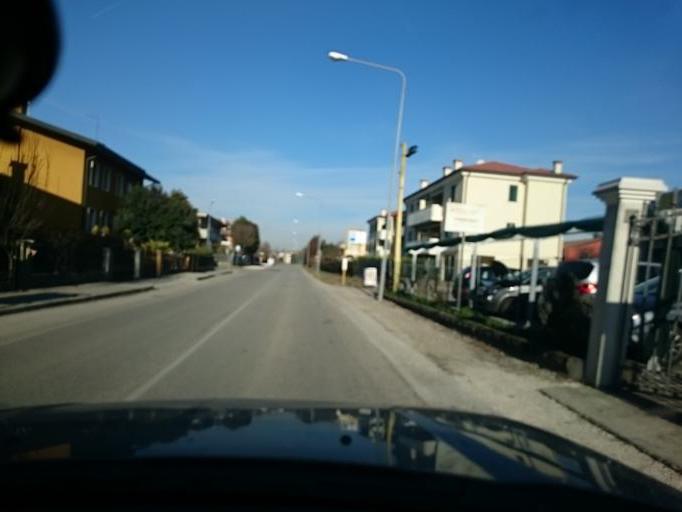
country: IT
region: Veneto
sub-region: Provincia di Venezia
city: Dolo
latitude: 45.4161
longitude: 12.0820
